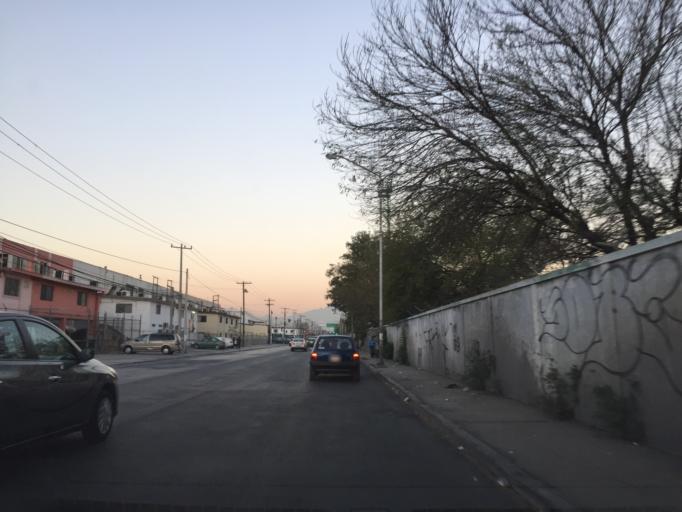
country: MX
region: Nuevo Leon
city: Guadalupe
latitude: 25.6953
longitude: -100.2242
